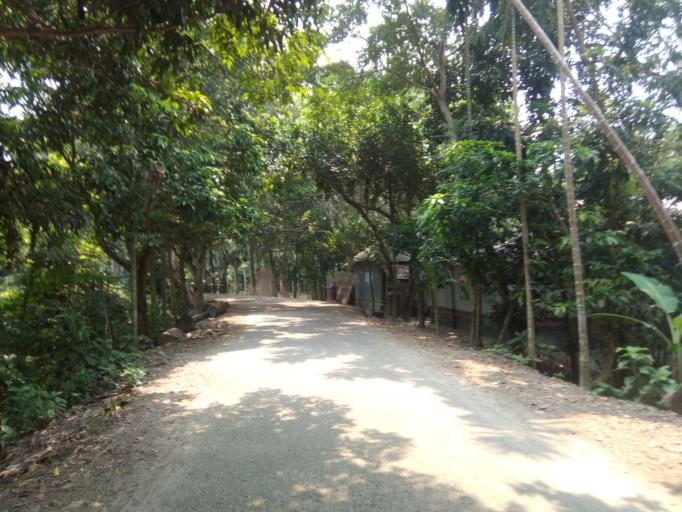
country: BD
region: Khulna
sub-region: Magura
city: Magura
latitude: 23.4482
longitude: 89.6236
